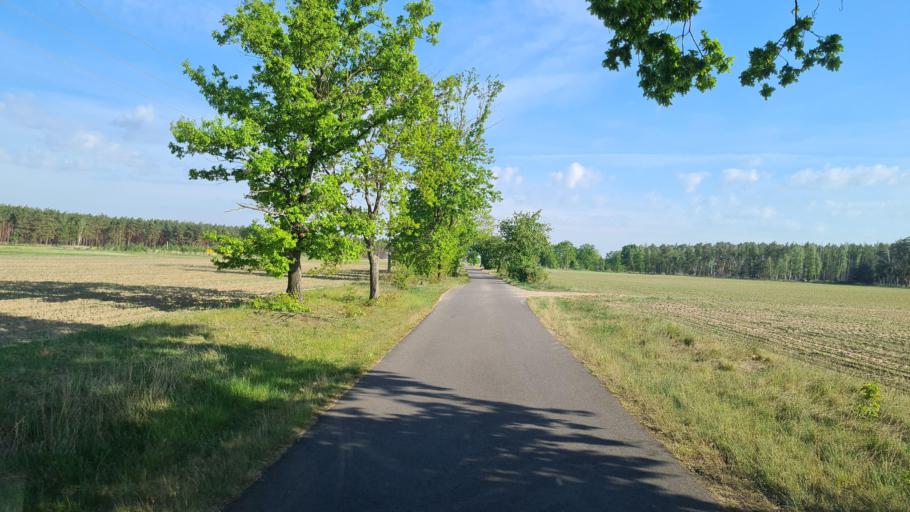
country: DE
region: Brandenburg
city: Falkenberg
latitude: 51.5973
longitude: 13.2045
